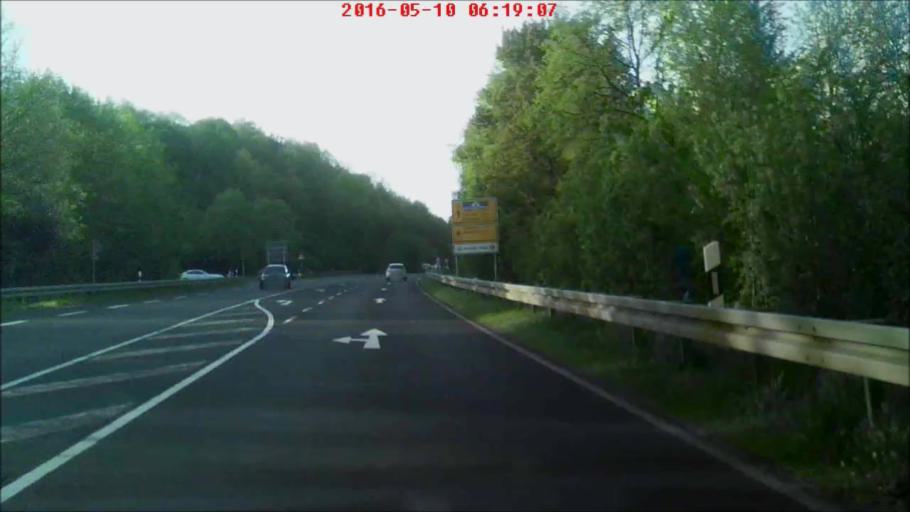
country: DE
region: Hesse
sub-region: Regierungsbezirk Kassel
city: Burghaun
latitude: 50.7147
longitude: 9.7172
